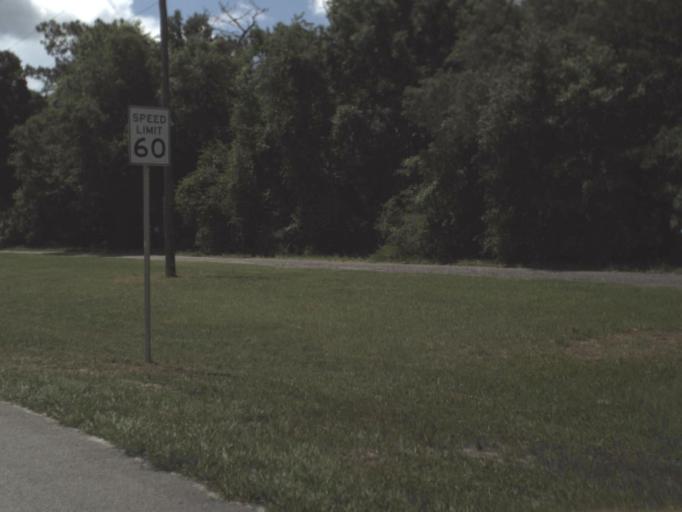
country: US
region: Florida
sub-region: Putnam County
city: Palatka
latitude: 29.5201
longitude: -81.6244
